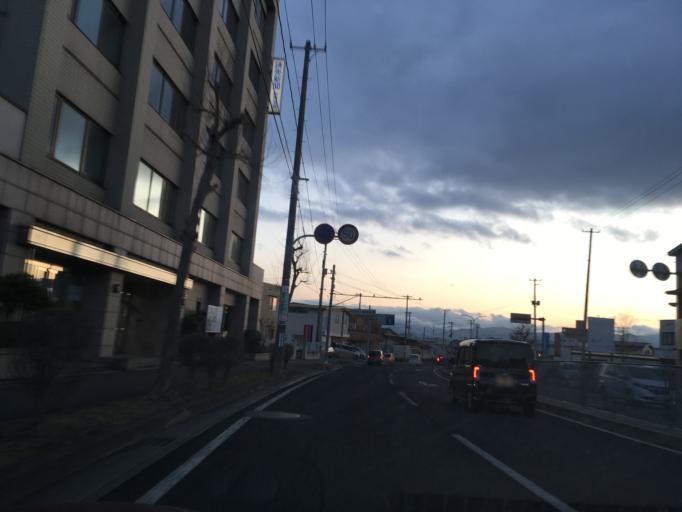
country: JP
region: Yamagata
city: Yamagata-shi
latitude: 38.2357
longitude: 140.3533
